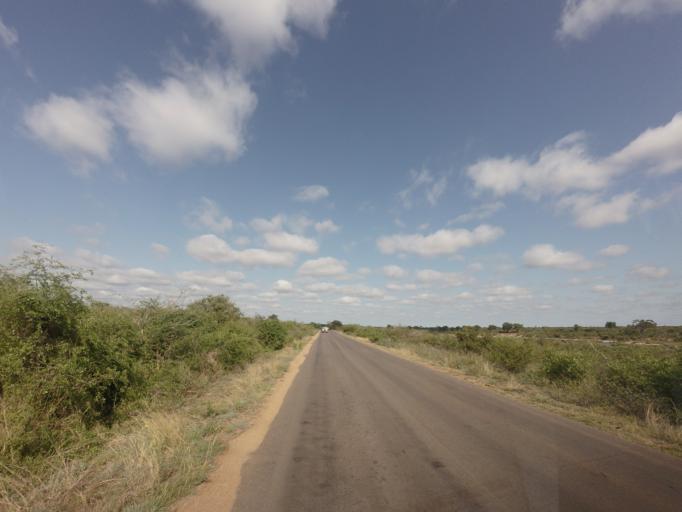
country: ZA
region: Mpumalanga
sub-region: Ehlanzeni District
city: Komatipoort
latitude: -25.1251
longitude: 31.9337
